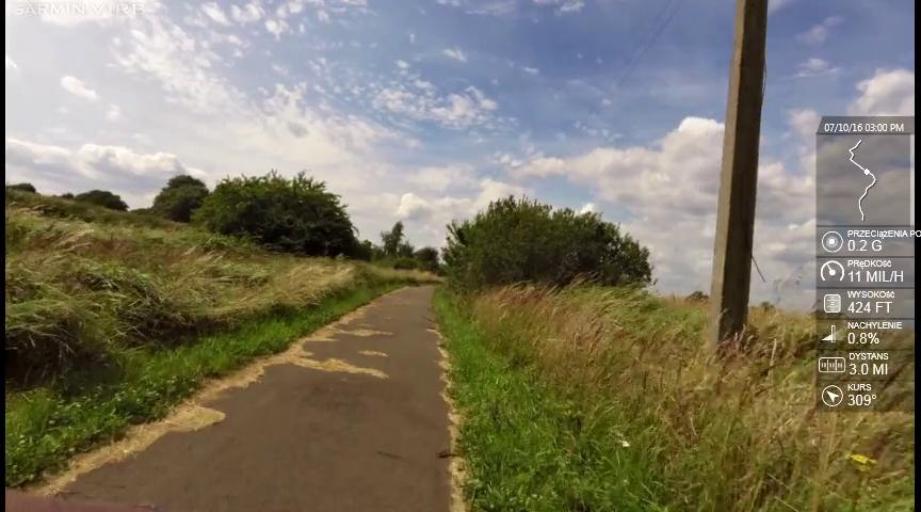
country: PL
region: West Pomeranian Voivodeship
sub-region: Powiat gryfinski
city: Banie
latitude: 53.1084
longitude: 14.6375
